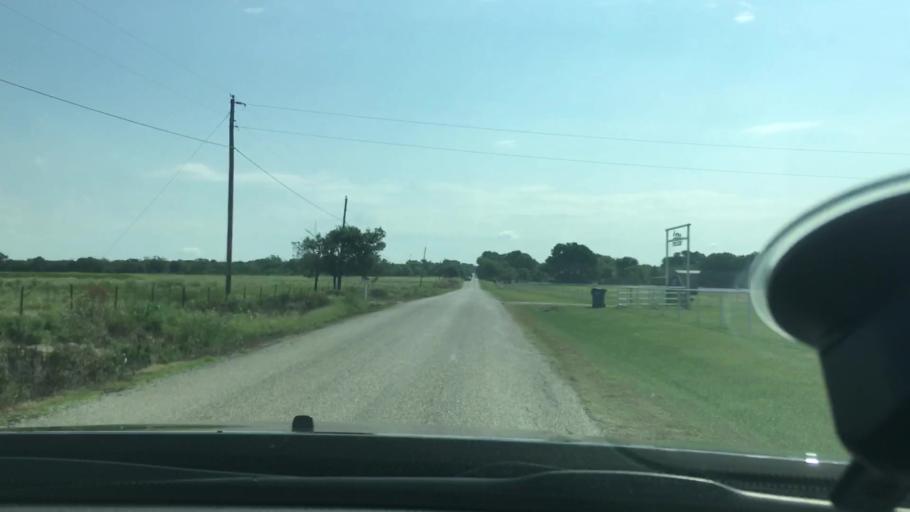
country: US
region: Oklahoma
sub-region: Bryan County
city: Colbert
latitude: 33.9110
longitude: -96.4956
